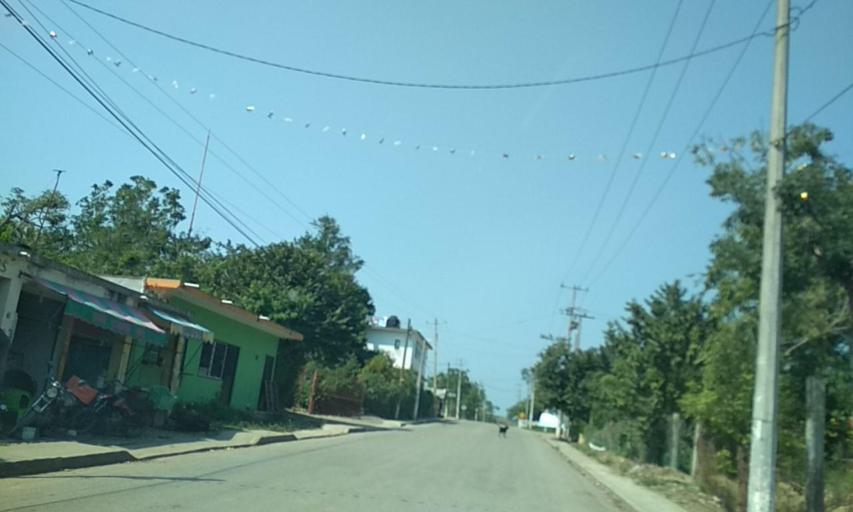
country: MX
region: Veracruz
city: Agua Dulce
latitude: 20.3715
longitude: -97.1789
